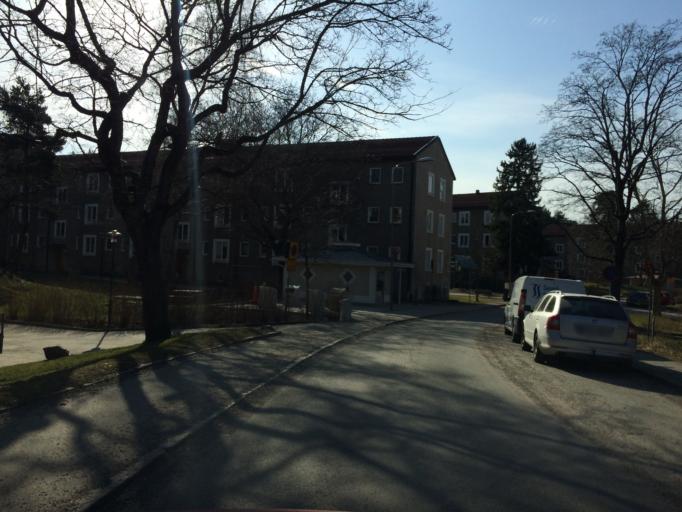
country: SE
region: Stockholm
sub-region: Stockholms Kommun
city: Arsta
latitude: 59.2889
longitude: 18.0019
